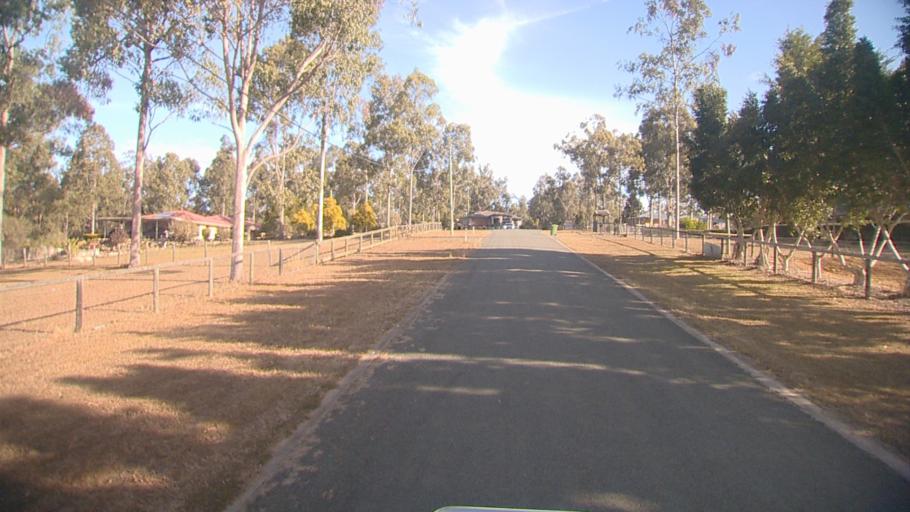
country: AU
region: Queensland
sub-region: Logan
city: Cedar Vale
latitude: -27.8757
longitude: 152.9982
